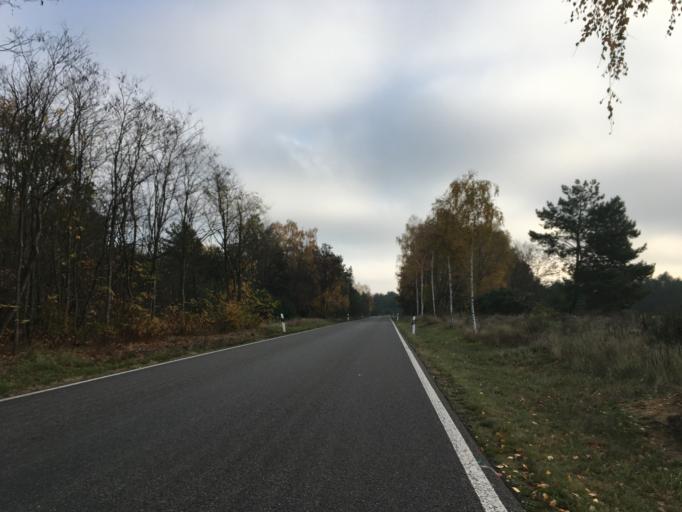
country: DE
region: Brandenburg
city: Halbe
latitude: 52.0324
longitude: 13.7579
